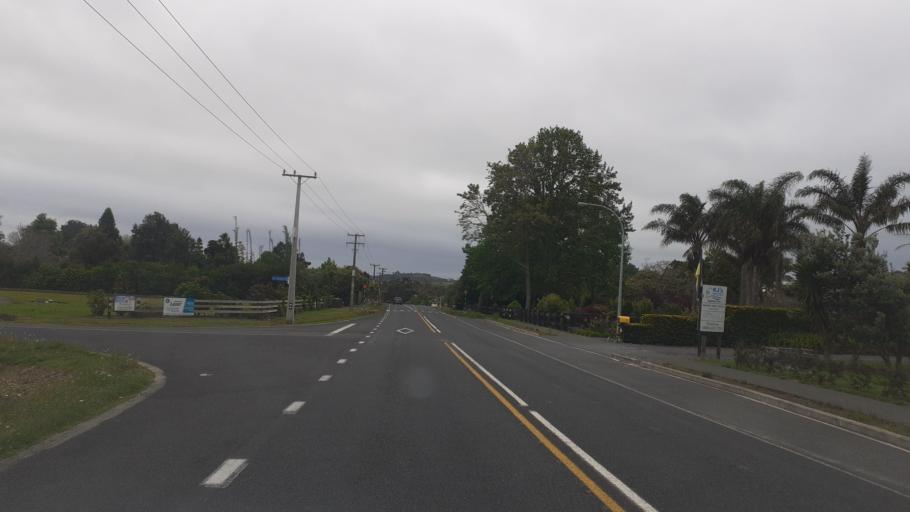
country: NZ
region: Northland
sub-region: Far North District
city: Kerikeri
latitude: -35.2082
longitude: 173.9643
